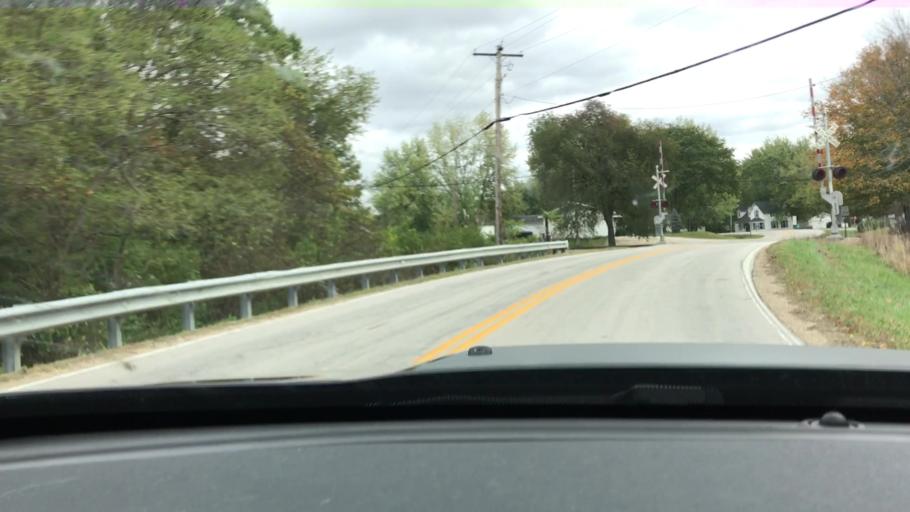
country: US
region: Illinois
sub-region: LaSalle County
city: Sheridan
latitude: 41.5308
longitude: -88.6908
